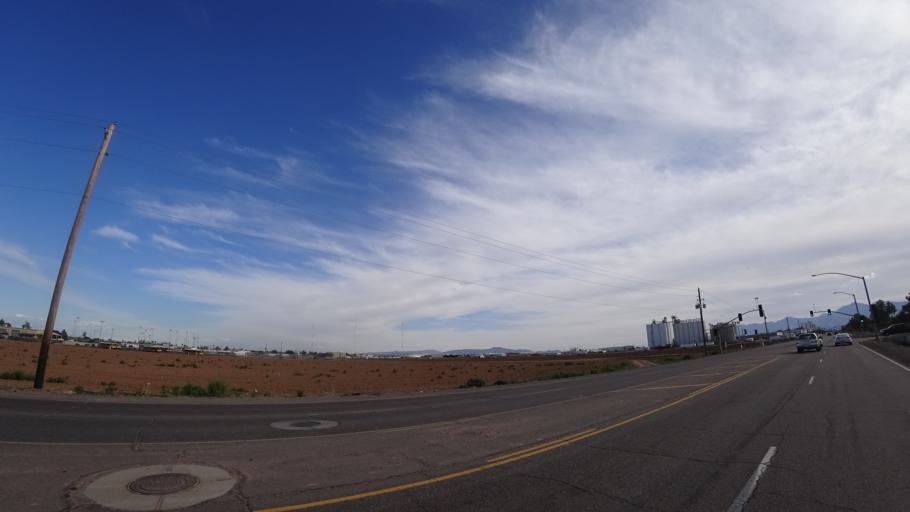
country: US
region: Arizona
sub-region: Maricopa County
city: Tolleson
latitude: 33.4477
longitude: -112.2725
